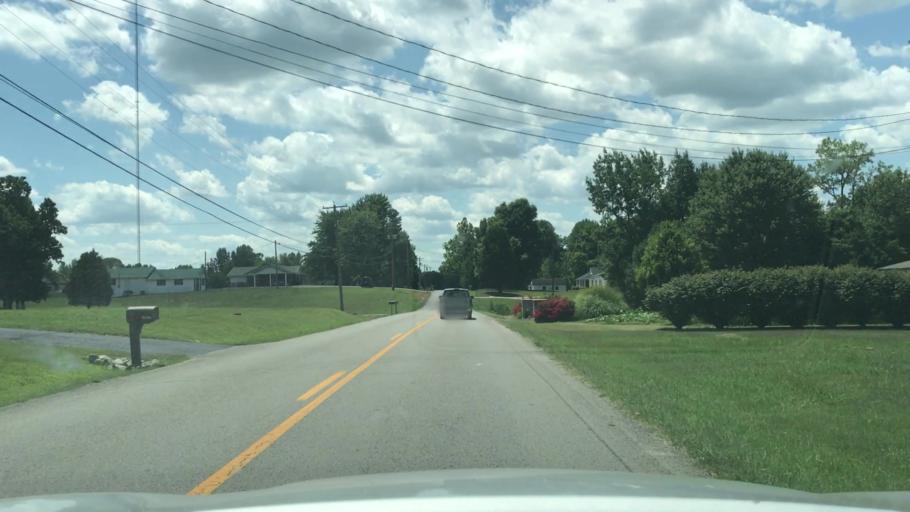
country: US
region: Kentucky
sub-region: Muhlenberg County
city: Greenville
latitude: 37.1966
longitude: -87.2108
